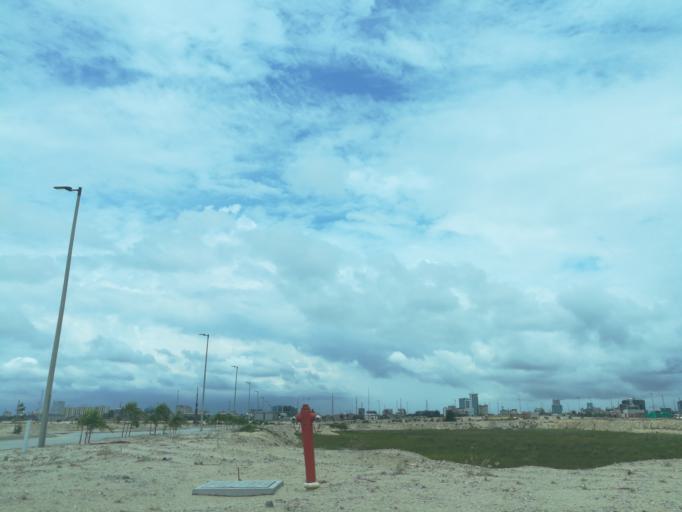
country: NG
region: Lagos
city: Ikoyi
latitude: 6.4118
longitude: 3.4244
